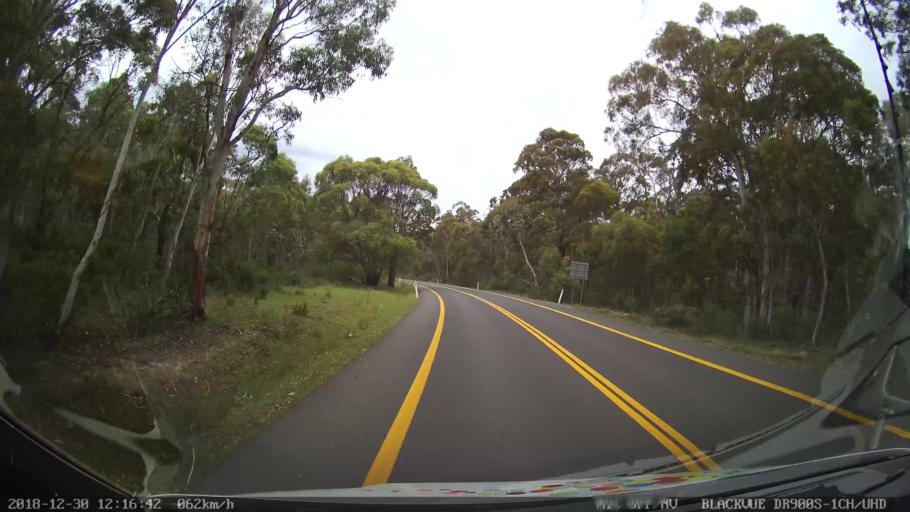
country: AU
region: New South Wales
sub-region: Snowy River
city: Jindabyne
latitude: -36.3474
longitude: 148.5637
